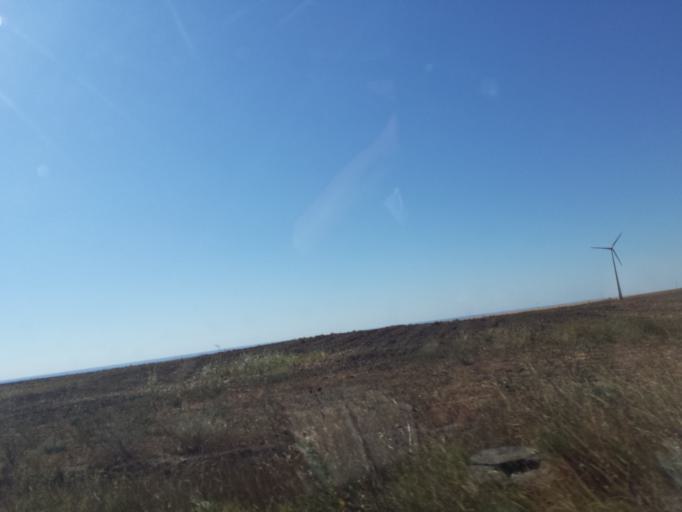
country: RO
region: Constanta
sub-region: Comuna Saraiu
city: Saraiu
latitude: 44.8024
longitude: 28.2462
